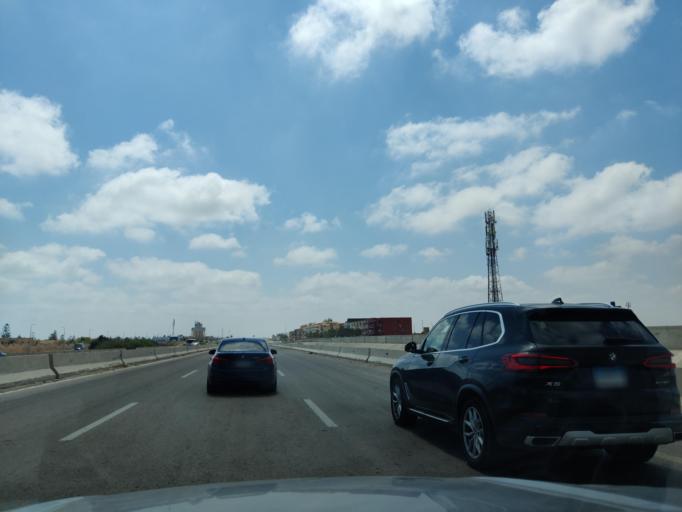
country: EG
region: Muhafazat Matruh
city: Al `Alamayn
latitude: 30.8200
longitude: 29.0190
